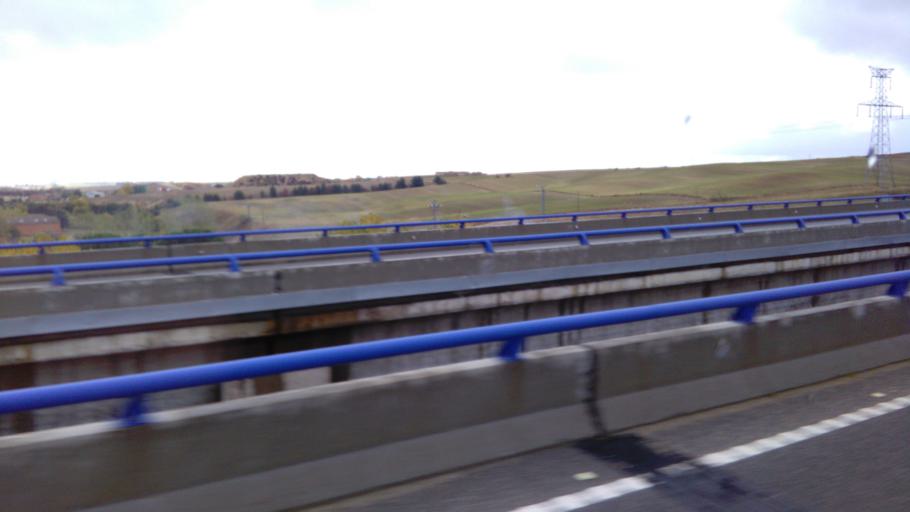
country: ES
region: Madrid
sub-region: Provincia de Madrid
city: Arroyomolinos
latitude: 40.2610
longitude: -3.9056
